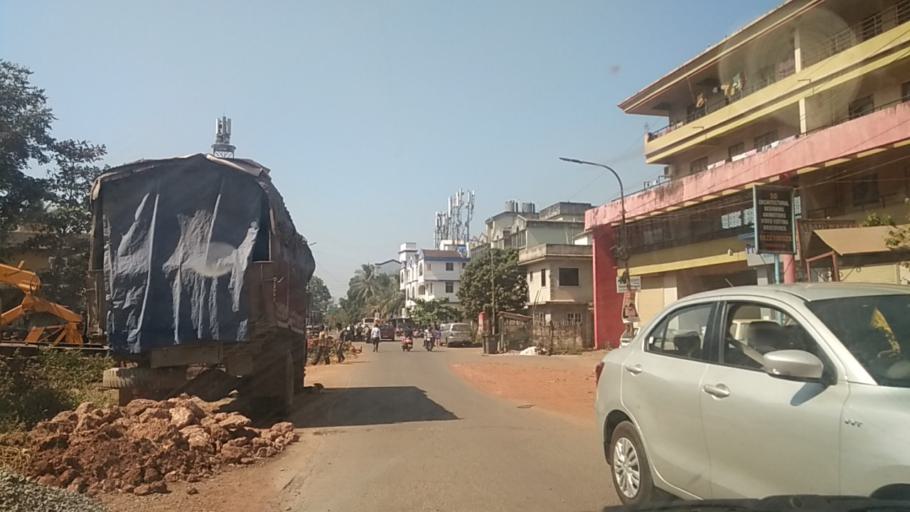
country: IN
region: Goa
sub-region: South Goa
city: Raia
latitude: 15.2996
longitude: 73.9652
